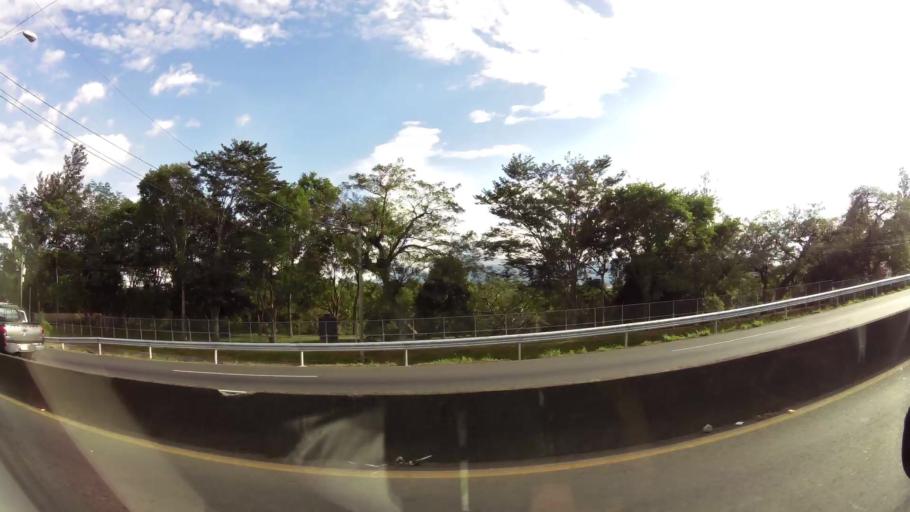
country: CR
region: Heredia
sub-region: Canton de Belen
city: San Antonio
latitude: 10.0024
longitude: -84.1802
